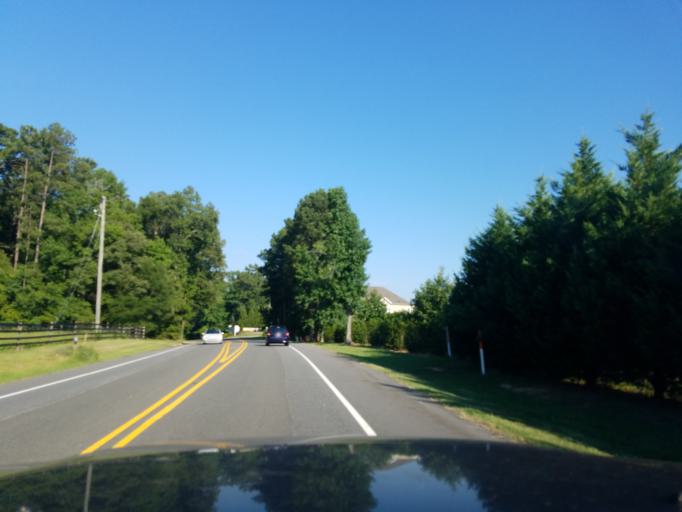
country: US
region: North Carolina
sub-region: Orange County
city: Chapel Hill
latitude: 35.8844
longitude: -78.9732
